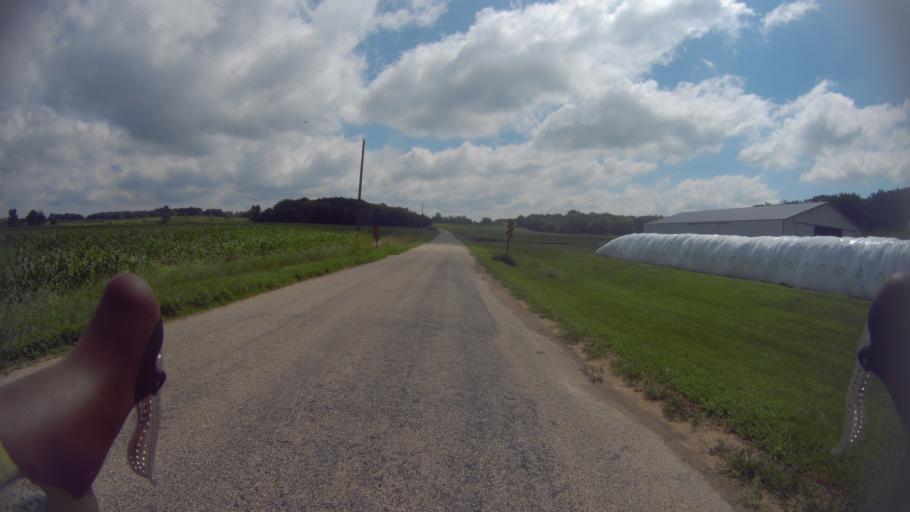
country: US
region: Wisconsin
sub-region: Columbia County
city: Lodi
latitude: 43.2276
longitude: -89.6094
